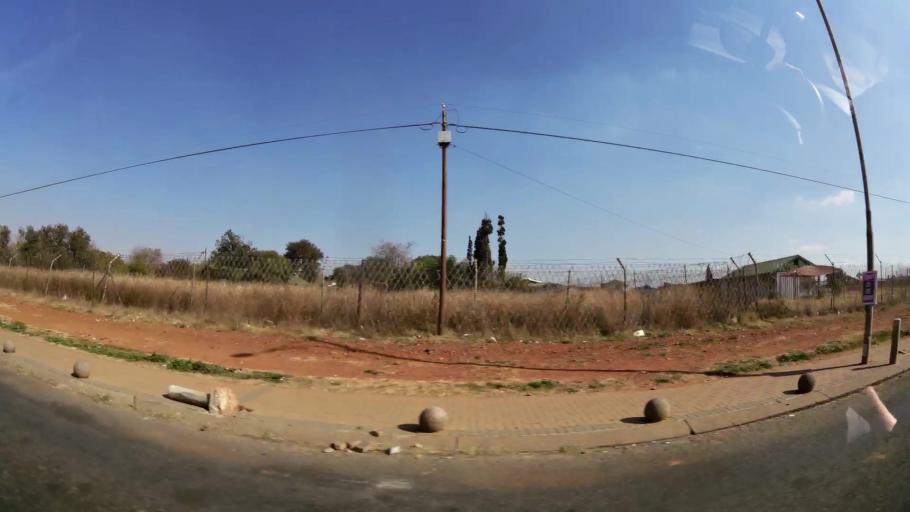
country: ZA
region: Gauteng
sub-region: City of Johannesburg Metropolitan Municipality
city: Roodepoort
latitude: -26.1617
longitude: 27.8016
